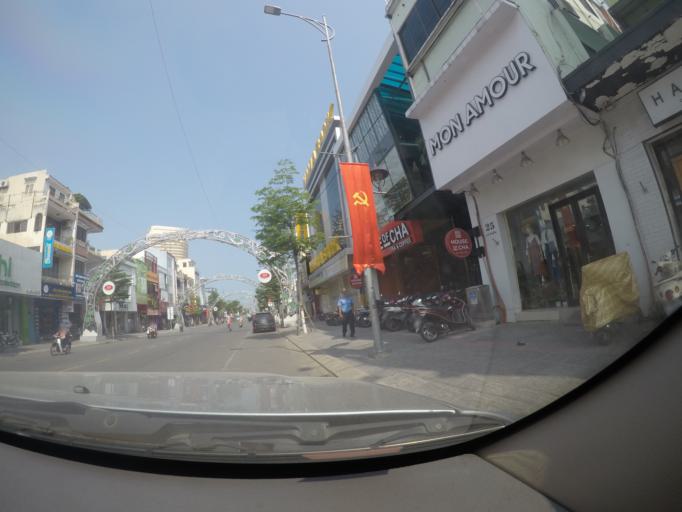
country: VN
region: Da Nang
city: Da Nang
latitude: 16.0715
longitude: 108.2212
